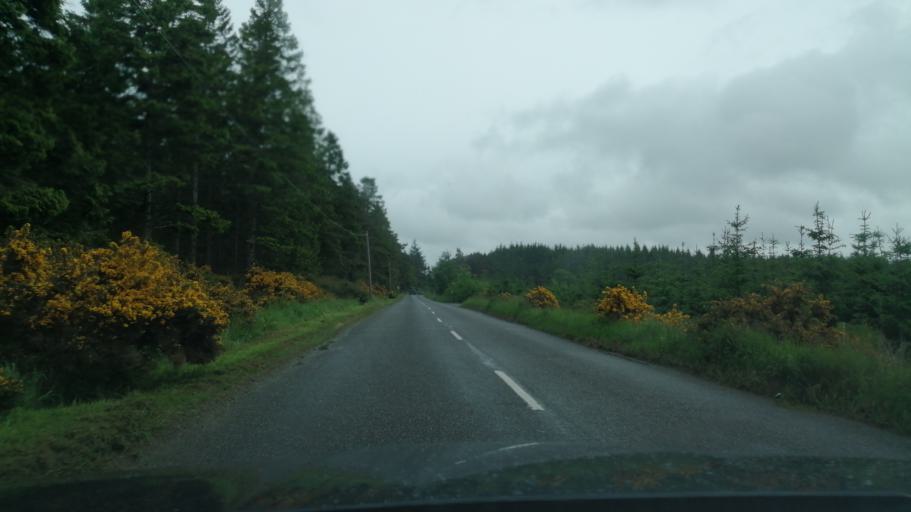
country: GB
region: Scotland
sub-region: Aberdeenshire
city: Portsoy
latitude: 57.6241
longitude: -2.7208
